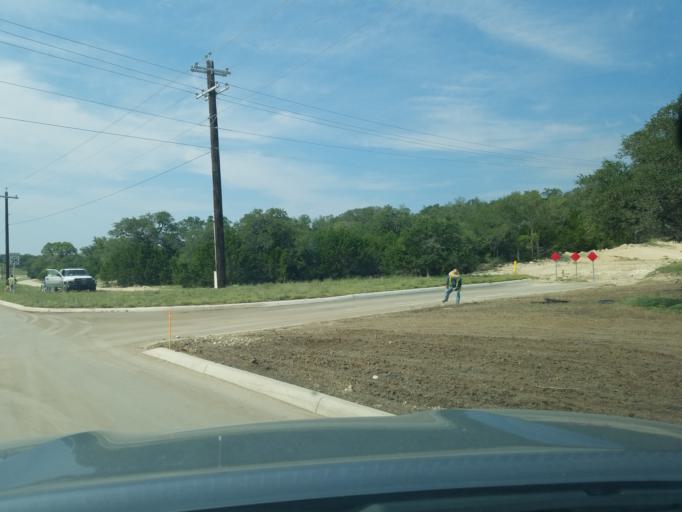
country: US
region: Texas
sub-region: Kendall County
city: Boerne
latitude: 29.7562
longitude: -98.7192
